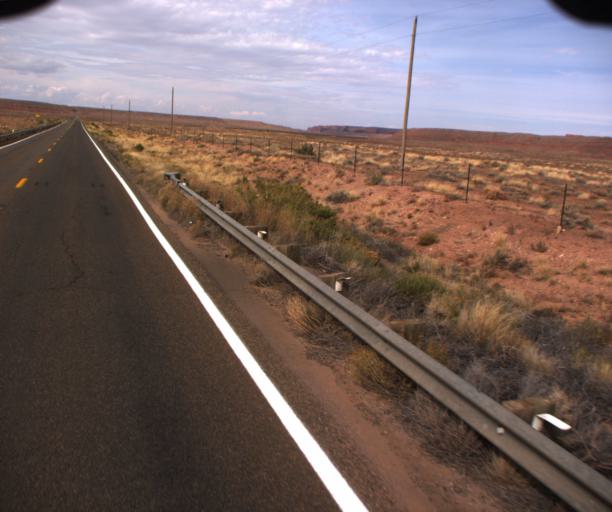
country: US
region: Arizona
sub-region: Apache County
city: Many Farms
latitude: 36.5223
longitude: -109.4938
